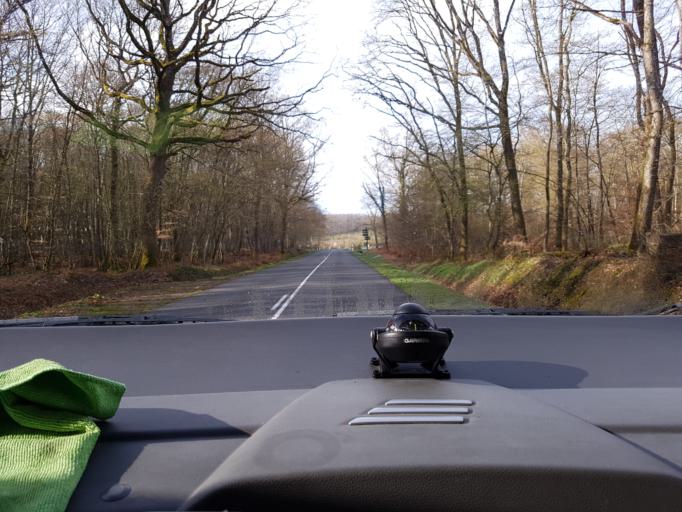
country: FR
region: Bourgogne
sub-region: Departement de Saone-et-Loire
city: Etang-sur-Arroux
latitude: 46.7943
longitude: 4.1493
